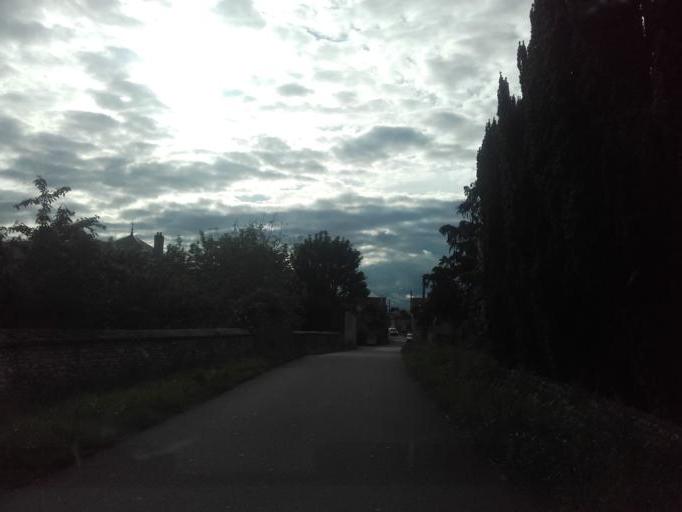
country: FR
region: Bourgogne
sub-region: Departement de Saone-et-Loire
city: Mellecey
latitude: 46.8316
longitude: 4.7393
